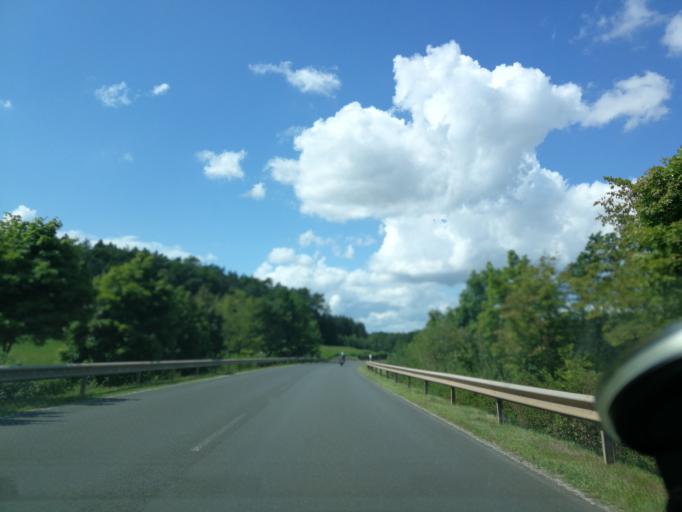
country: DE
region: Rheinland-Pfalz
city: Binsfeld
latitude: 49.9631
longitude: 6.7263
